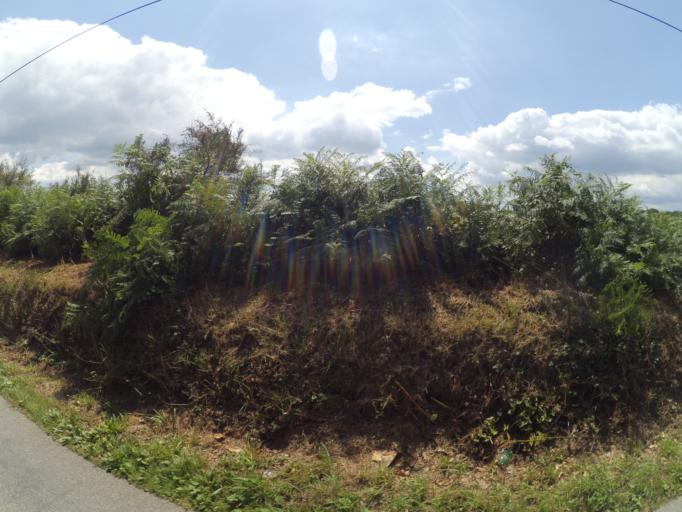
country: FR
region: Brittany
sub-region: Departement du Morbihan
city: Landaul
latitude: 47.7345
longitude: -3.0471
